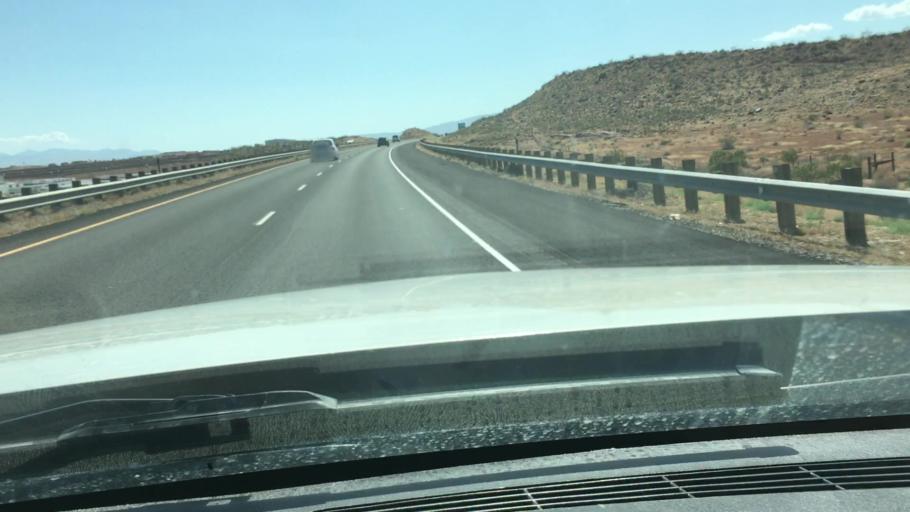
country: US
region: Utah
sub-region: Washington County
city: Washington
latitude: 37.1784
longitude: -113.4220
